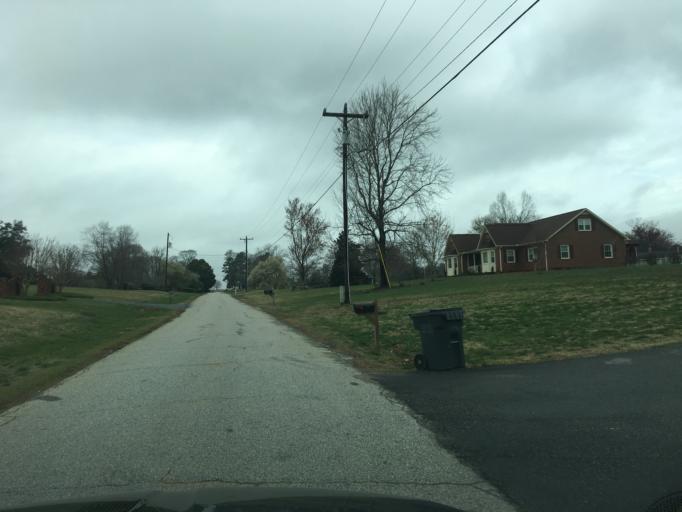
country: US
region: South Carolina
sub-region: Spartanburg County
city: Inman Mills
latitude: 35.0203
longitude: -82.1097
